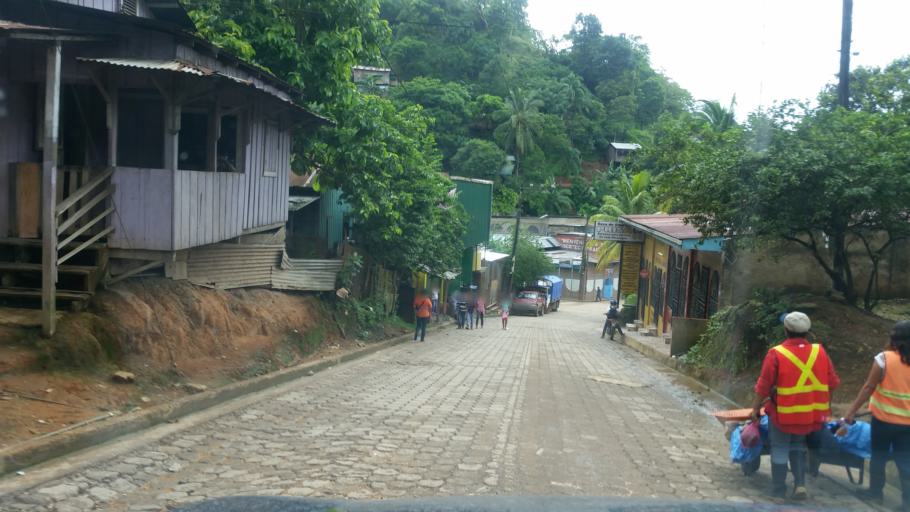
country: NI
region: Atlantico Norte (RAAN)
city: Bonanza
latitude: 14.0294
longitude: -84.5970
